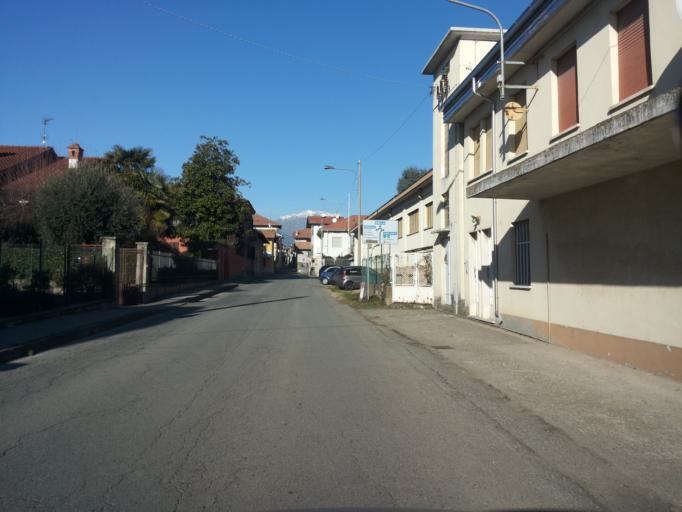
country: IT
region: Piedmont
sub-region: Provincia di Biella
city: Ponderano
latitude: 45.5343
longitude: 8.0561
